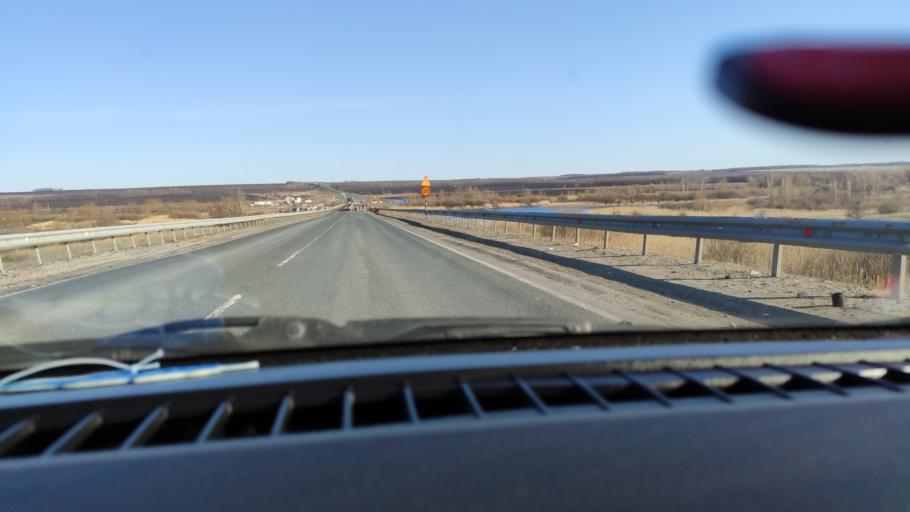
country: RU
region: Saratov
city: Dukhovnitskoye
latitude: 52.7353
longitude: 48.2566
